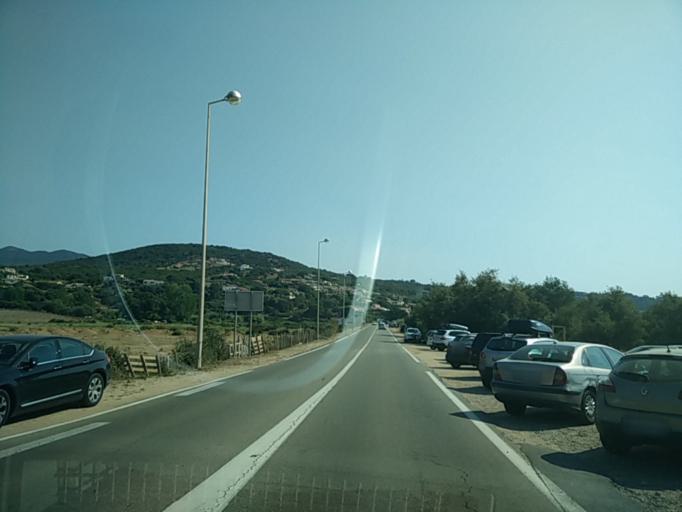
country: FR
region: Corsica
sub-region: Departement de la Corse-du-Sud
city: Pietrosella
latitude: 41.8547
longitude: 8.7911
